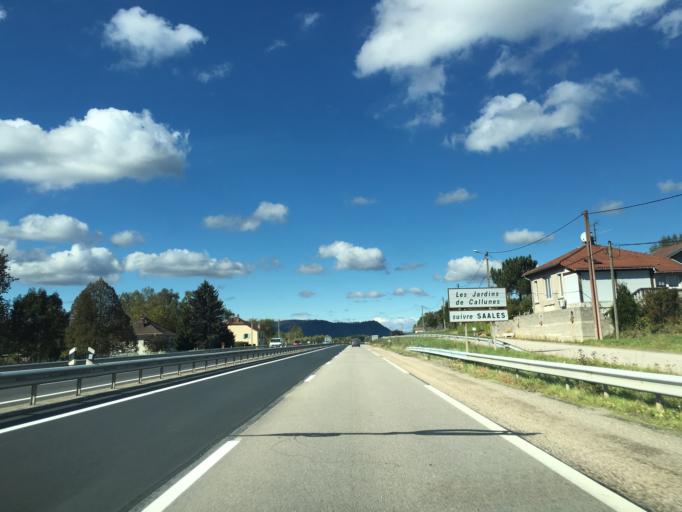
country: FR
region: Lorraine
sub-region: Departement des Vosges
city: Saint-Michel-sur-Meurthe
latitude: 48.3343
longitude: 6.8950
